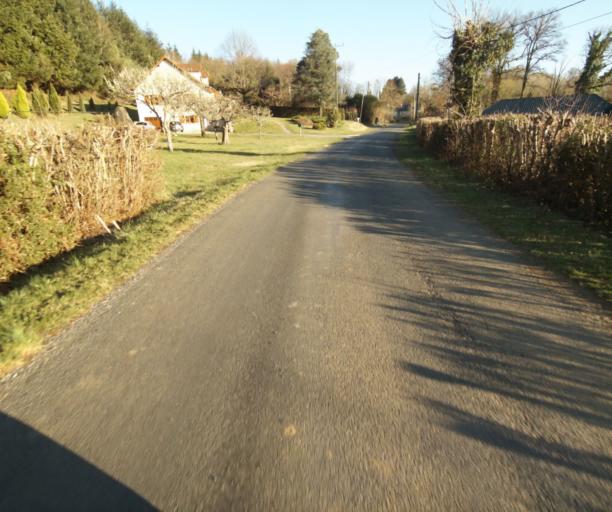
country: FR
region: Limousin
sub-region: Departement de la Correze
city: Seilhac
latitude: 45.3566
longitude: 1.7051
